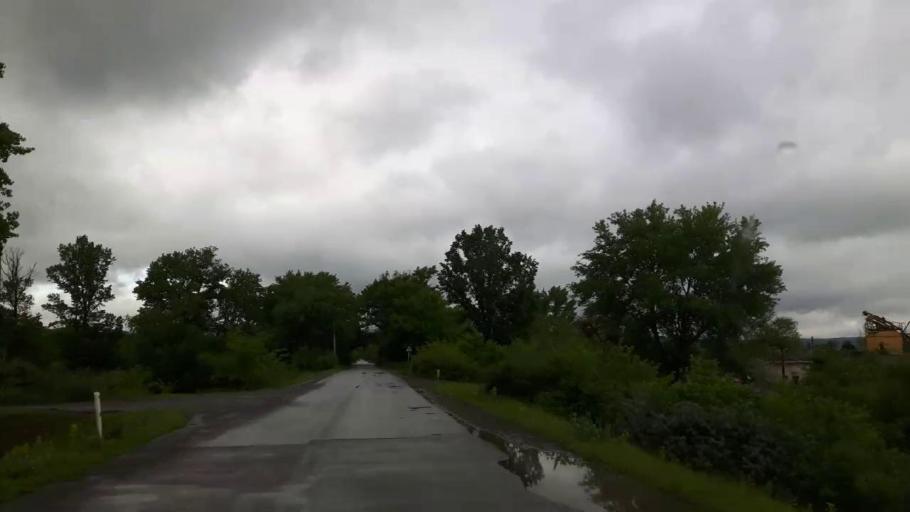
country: GE
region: Shida Kartli
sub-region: Khashuris Raioni
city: Khashuri
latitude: 41.9956
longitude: 43.6562
